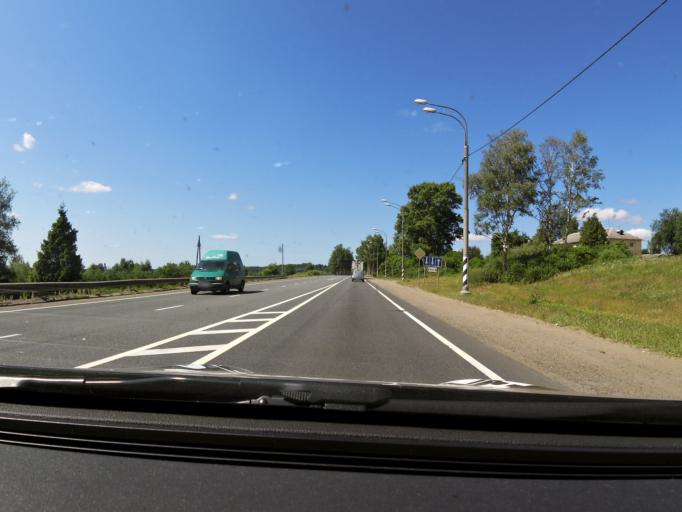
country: RU
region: Novgorod
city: Valday
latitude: 58.0345
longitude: 32.9697
